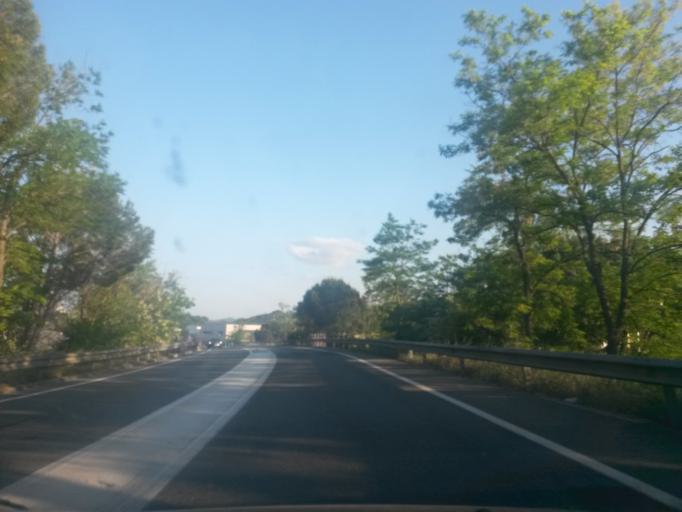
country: ES
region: Catalonia
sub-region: Provincia de Girona
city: Cornella del Terri
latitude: 42.0976
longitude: 2.7978
